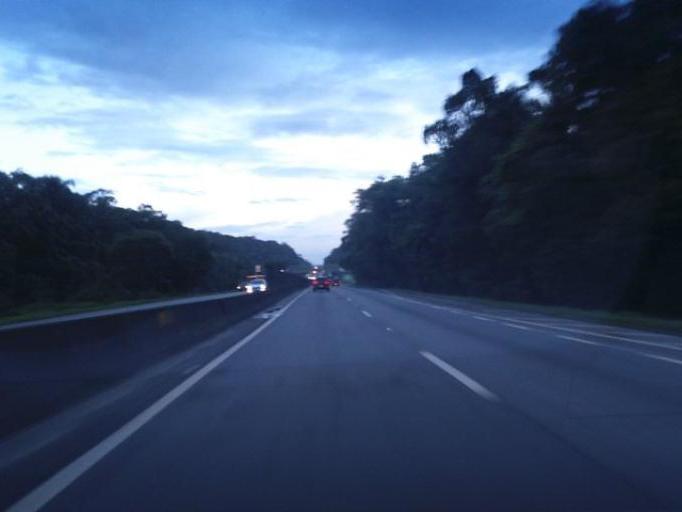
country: BR
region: Santa Catarina
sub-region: Joinville
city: Joinville
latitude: -26.2155
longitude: -48.9160
